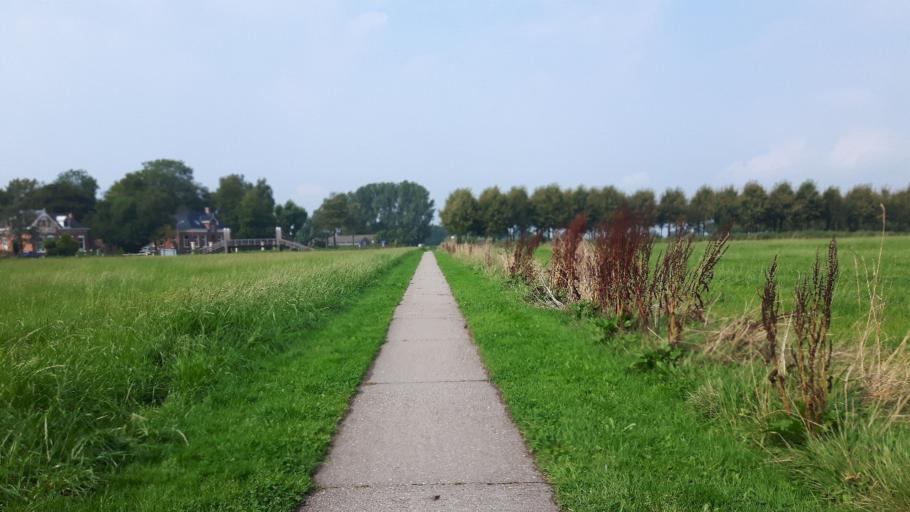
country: NL
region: Groningen
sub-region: Gemeente Bedum
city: Bedum
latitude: 53.3507
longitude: 6.6447
